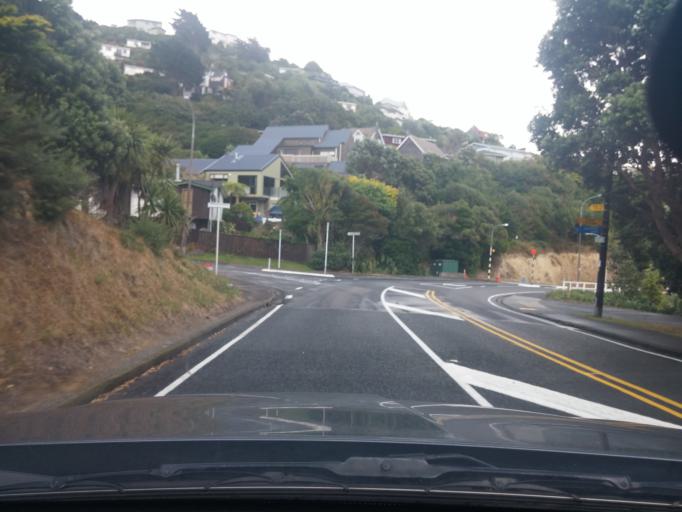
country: NZ
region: Wellington
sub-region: Wellington City
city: Kelburn
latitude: -41.2581
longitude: 174.7659
